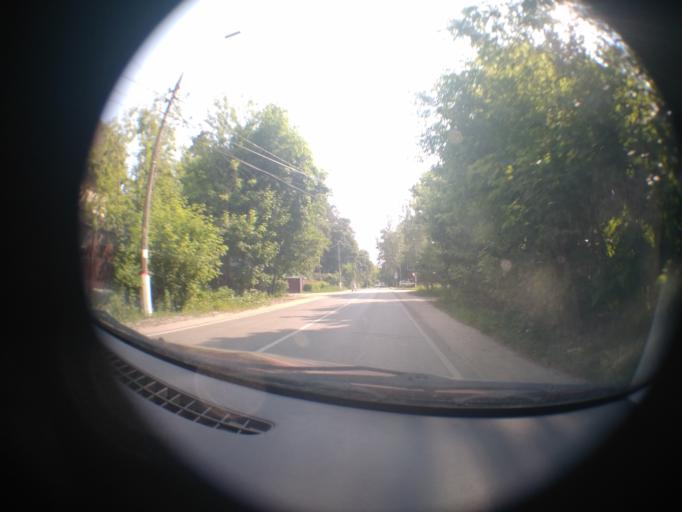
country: RU
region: Moskovskaya
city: Zhukovskiy
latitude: 55.5859
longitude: 38.1488
